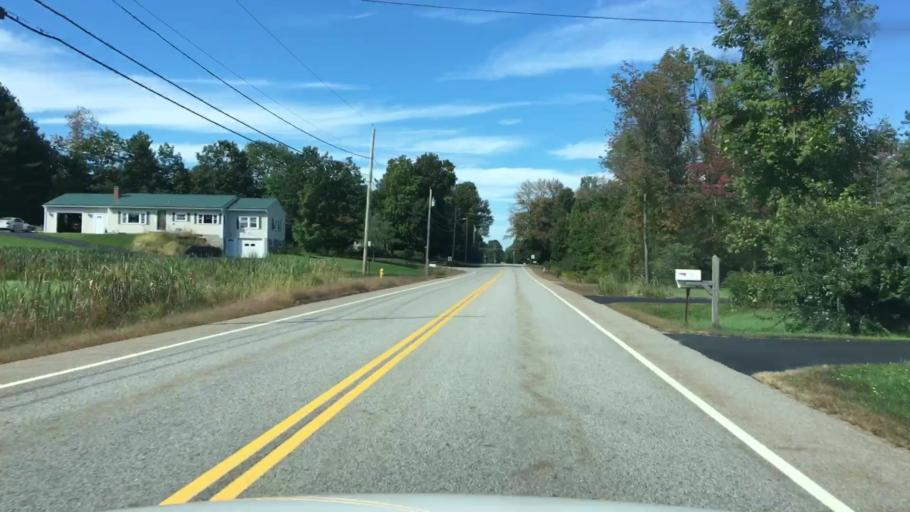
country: US
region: Maine
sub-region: Cumberland County
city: Gorham
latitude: 43.6691
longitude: -70.4084
